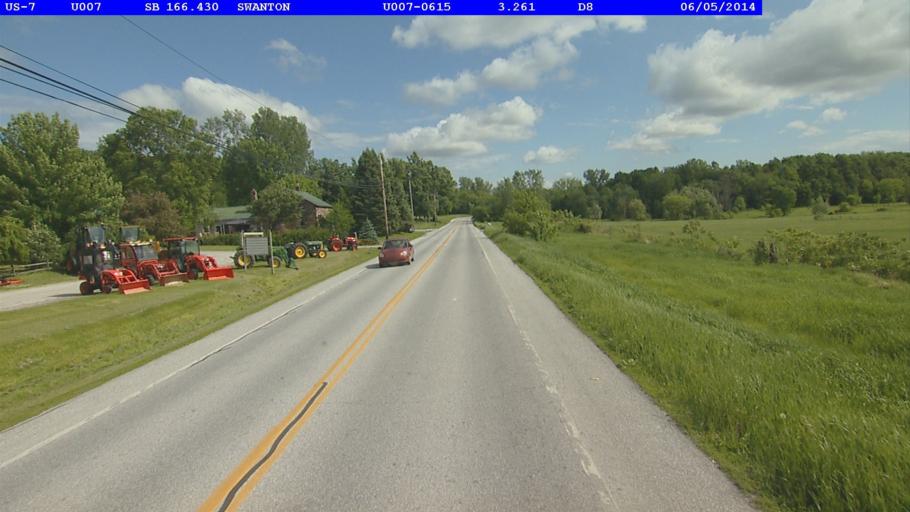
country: US
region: Vermont
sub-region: Franklin County
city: Swanton
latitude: 44.8930
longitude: -73.0918
